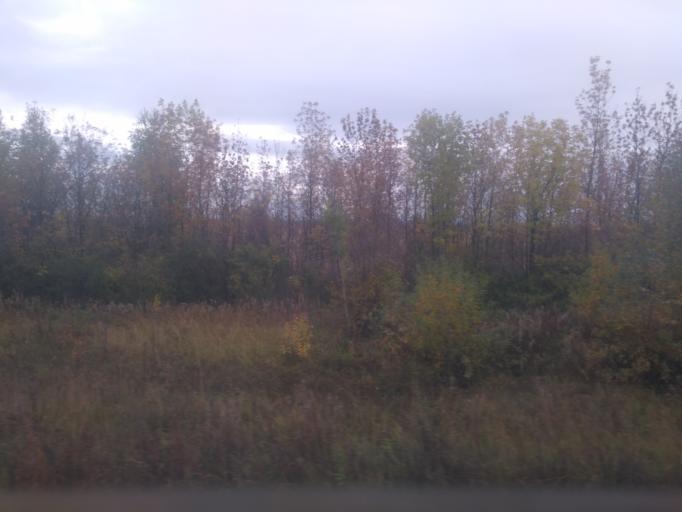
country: RU
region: Udmurtiya
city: Alnashi
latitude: 56.2082
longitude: 52.6231
